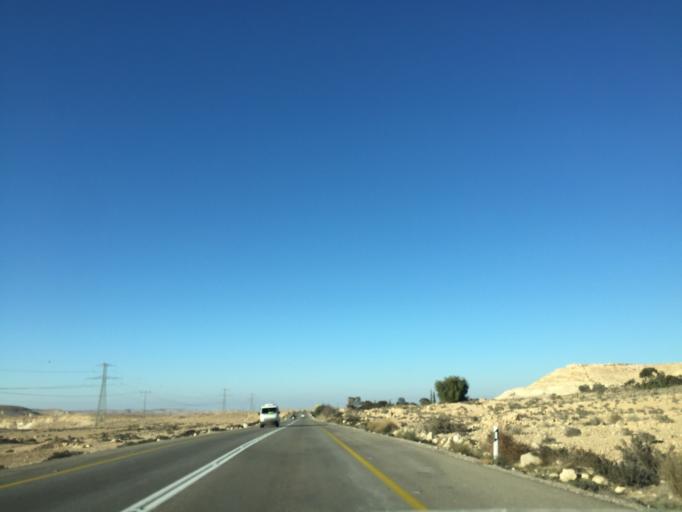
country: IL
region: Southern District
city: Midreshet Ben-Gurion
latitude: 30.7823
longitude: 34.7688
